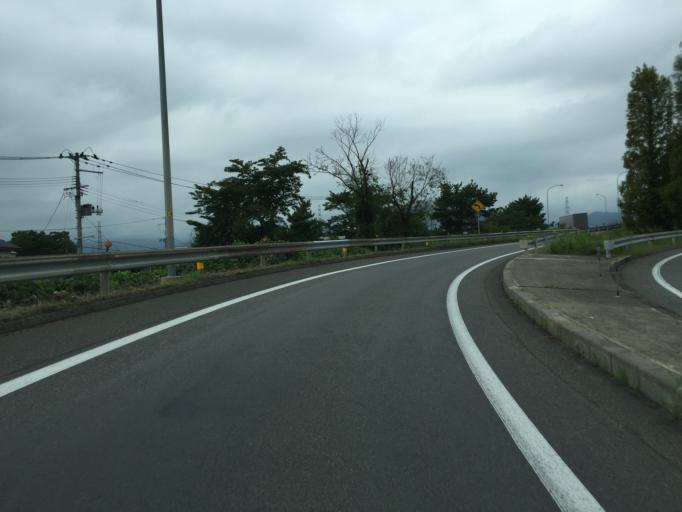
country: JP
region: Fukushima
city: Fukushima-shi
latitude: 37.8018
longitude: 140.4554
